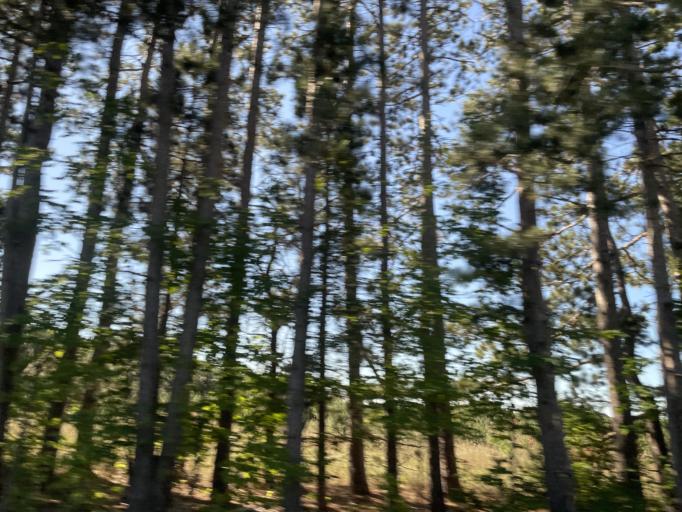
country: US
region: Michigan
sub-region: Benzie County
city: Beulah
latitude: 44.6173
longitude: -86.0646
